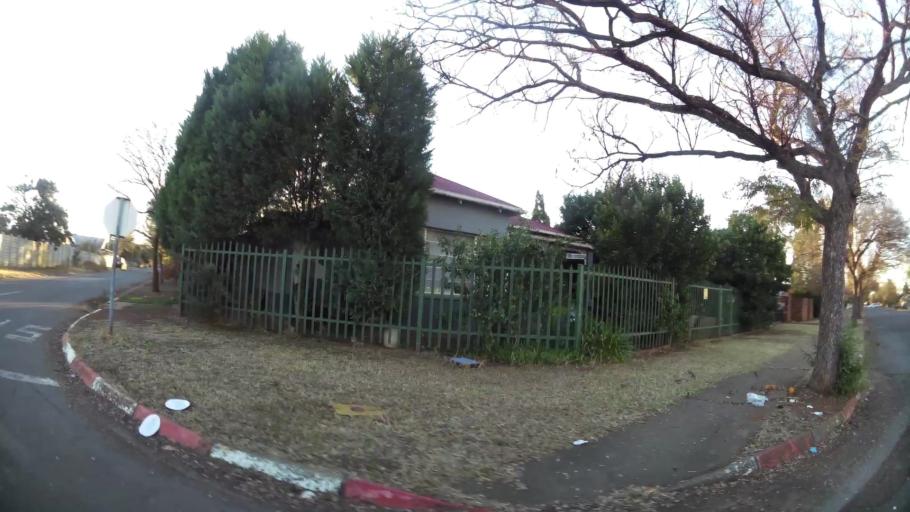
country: ZA
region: North-West
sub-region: Dr Kenneth Kaunda District Municipality
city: Potchefstroom
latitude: -26.7295
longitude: 27.0917
